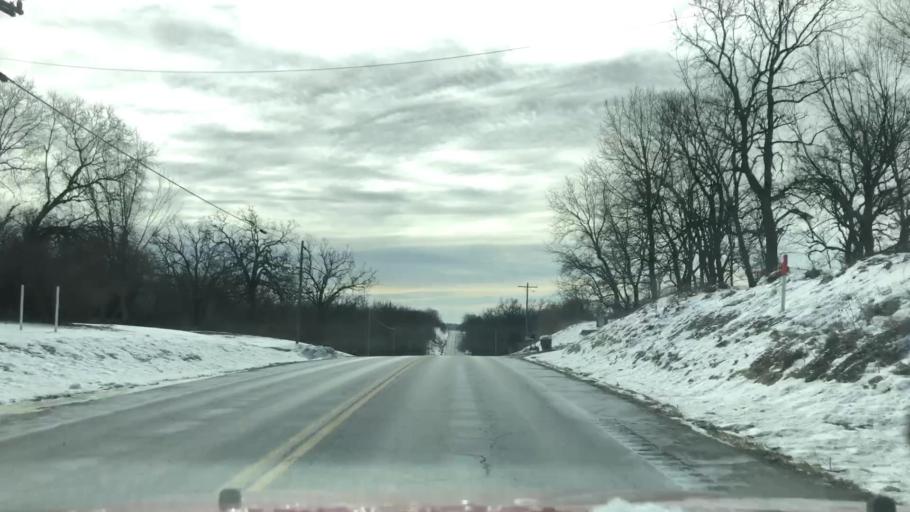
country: US
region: Missouri
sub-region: Jackson County
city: Oak Grove
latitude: 38.9743
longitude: -94.1306
